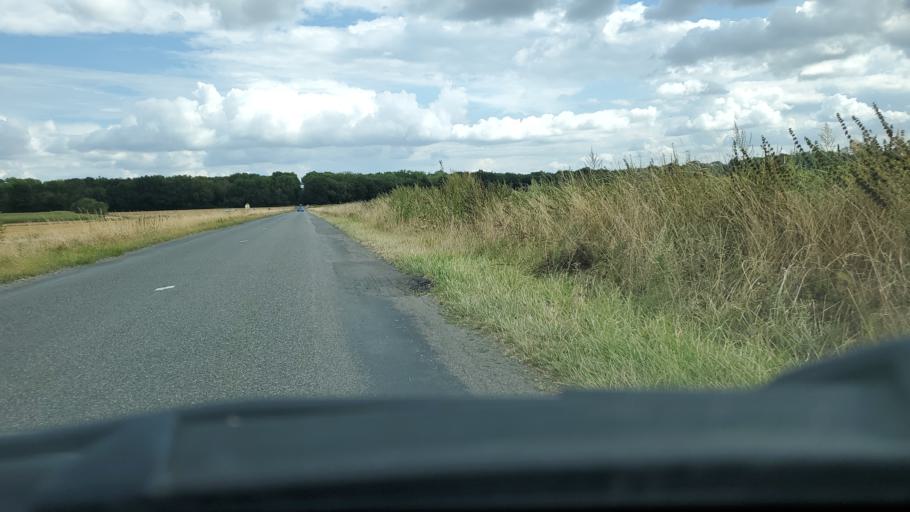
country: FR
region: Ile-de-France
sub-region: Departement de Seine-et-Marne
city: Pommeuse
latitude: 48.8631
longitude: 3.0039
